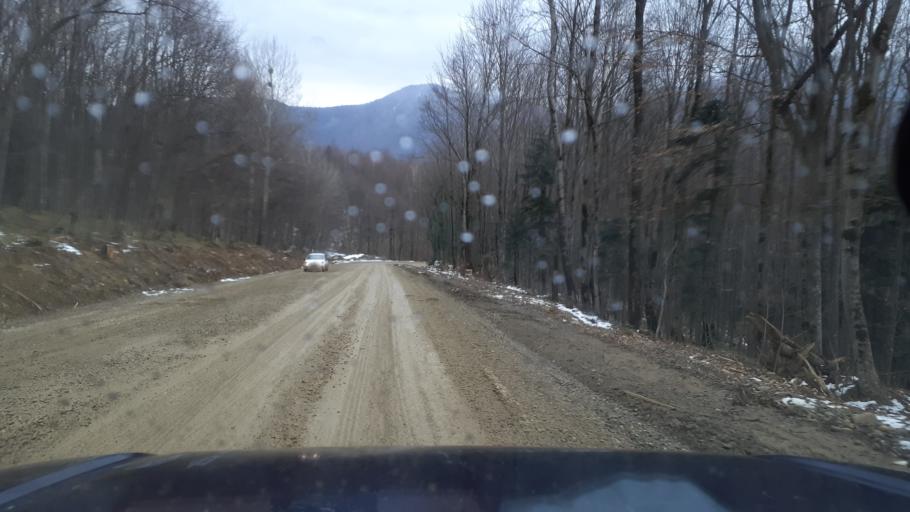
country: RU
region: Krasnodarskiy
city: Neftegorsk
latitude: 44.1647
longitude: 39.8051
